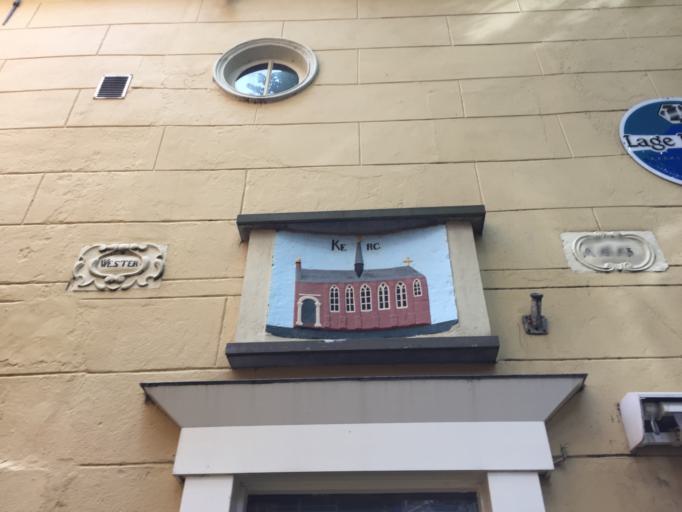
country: NL
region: Friesland
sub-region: Gemeente Leeuwarden
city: Bilgaard
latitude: 53.2017
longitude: 5.7942
